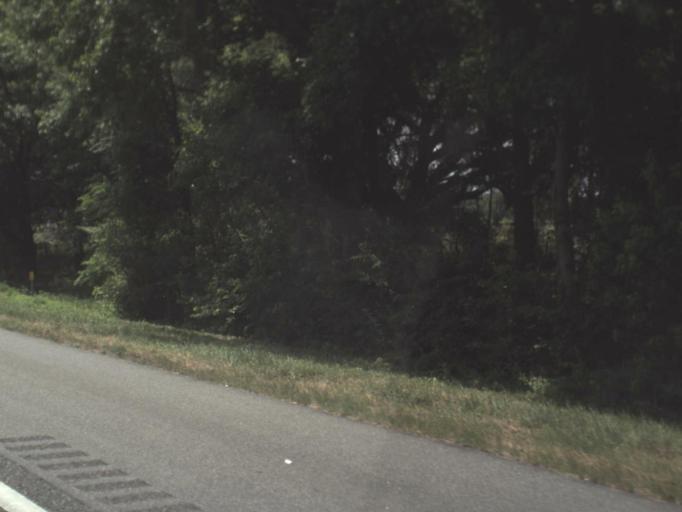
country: US
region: Florida
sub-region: Suwannee County
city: Wellborn
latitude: 30.2864
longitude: -82.7716
